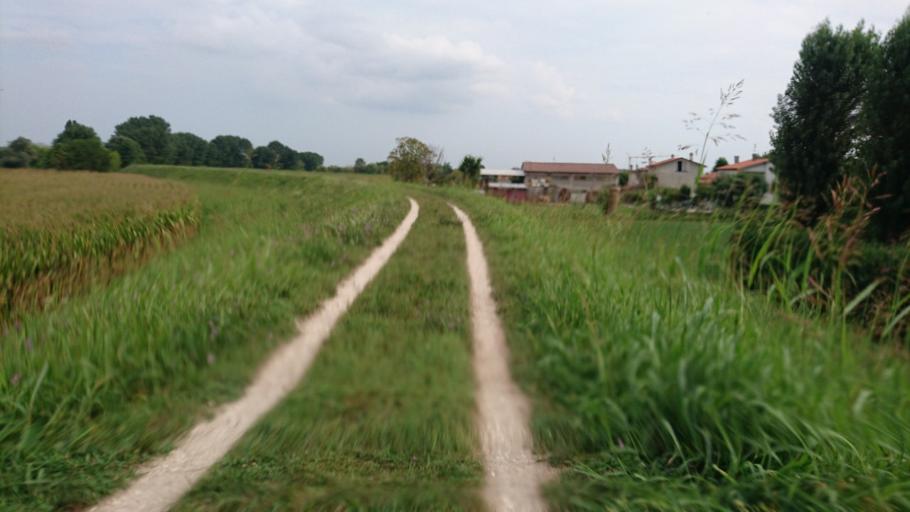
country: IT
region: Veneto
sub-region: Provincia di Padova
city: Saccolongo
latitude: 45.3979
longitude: 11.7630
